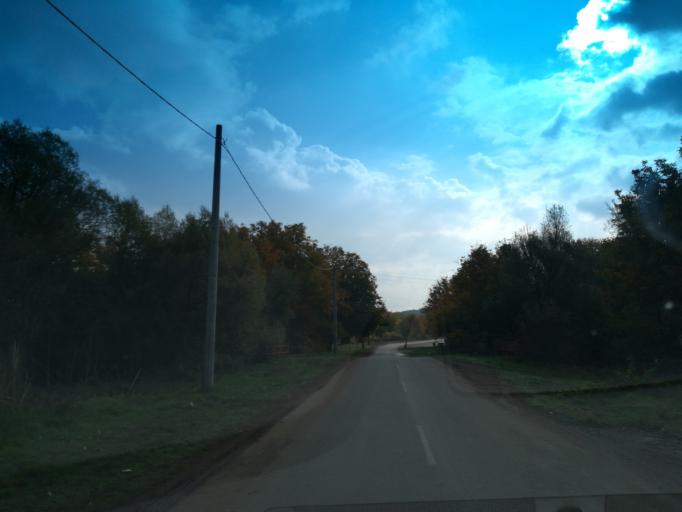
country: BG
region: Stara Zagora
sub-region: Obshtina Nikolaevo
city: Elkhovo
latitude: 42.3395
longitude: 25.4049
